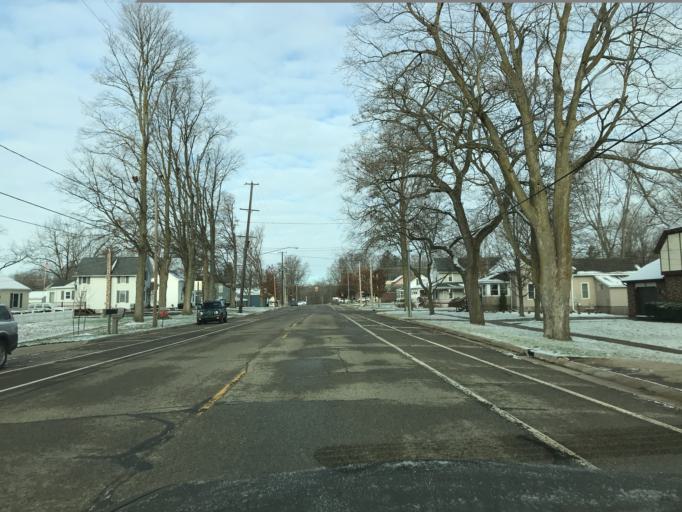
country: US
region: Michigan
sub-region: Eaton County
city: Dimondale
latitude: 42.6444
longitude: -84.6472
